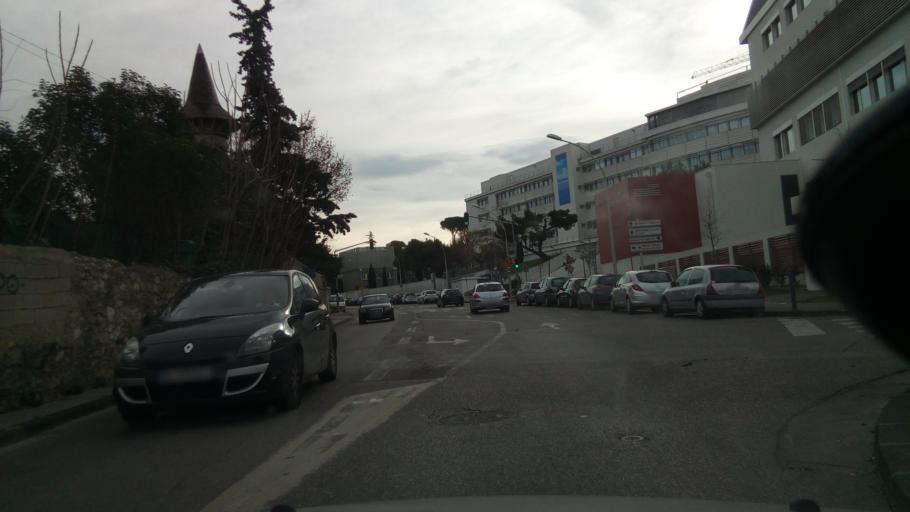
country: FR
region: Provence-Alpes-Cote d'Azur
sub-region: Departement des Bouches-du-Rhone
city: Marseille 09
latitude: 43.2637
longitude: 5.4105
